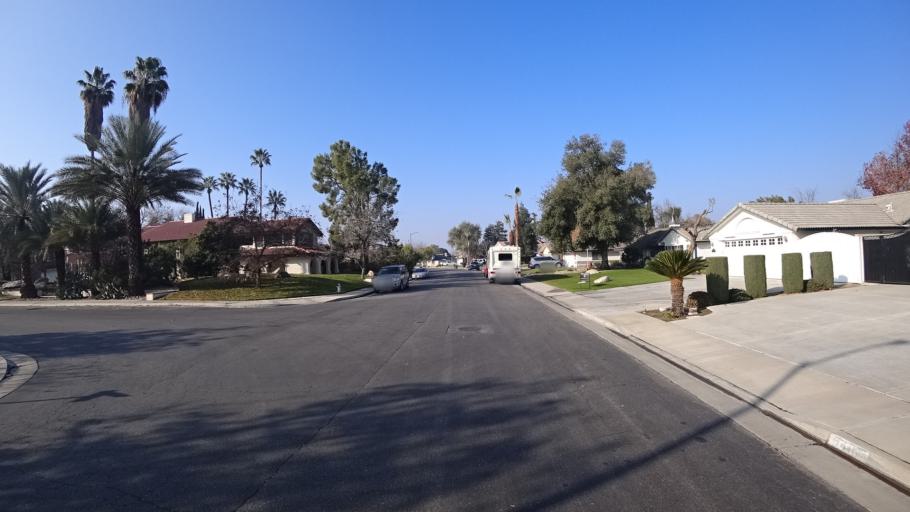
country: US
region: California
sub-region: Kern County
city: Greenacres
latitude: 35.3975
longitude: -119.1069
